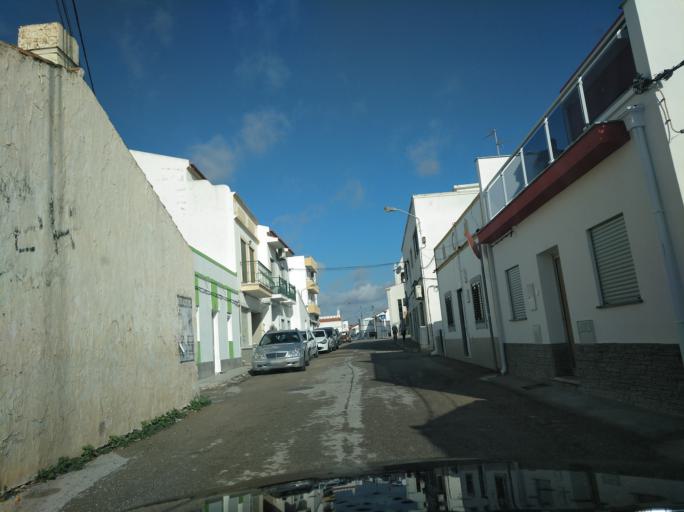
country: PT
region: Faro
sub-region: Vila Real de Santo Antonio
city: Monte Gordo
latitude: 37.1771
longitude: -7.5003
